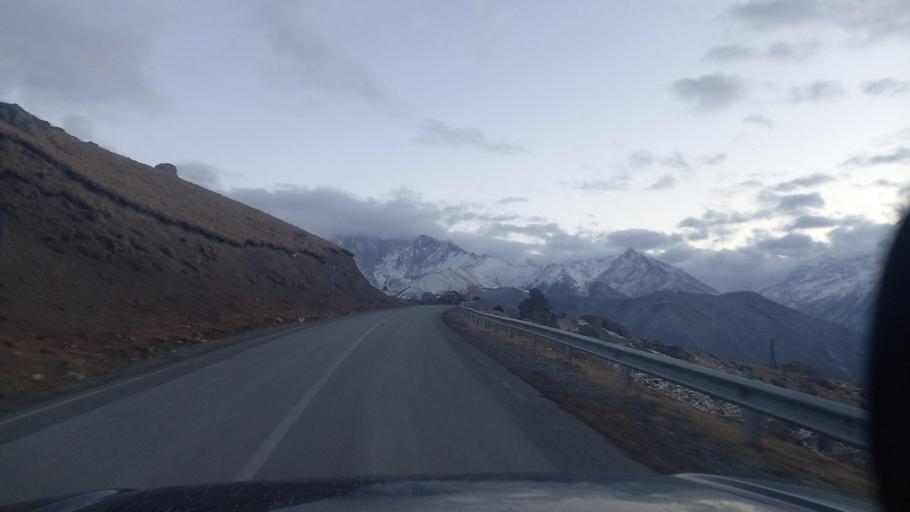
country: RU
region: Ingushetiya
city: Dzhayrakh
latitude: 42.8215
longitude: 44.8305
